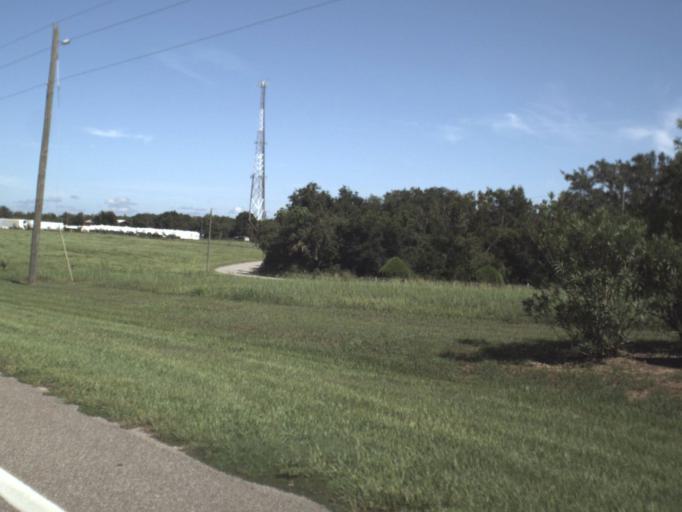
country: US
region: Florida
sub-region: Polk County
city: Polk City
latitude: 28.1795
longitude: -81.8175
